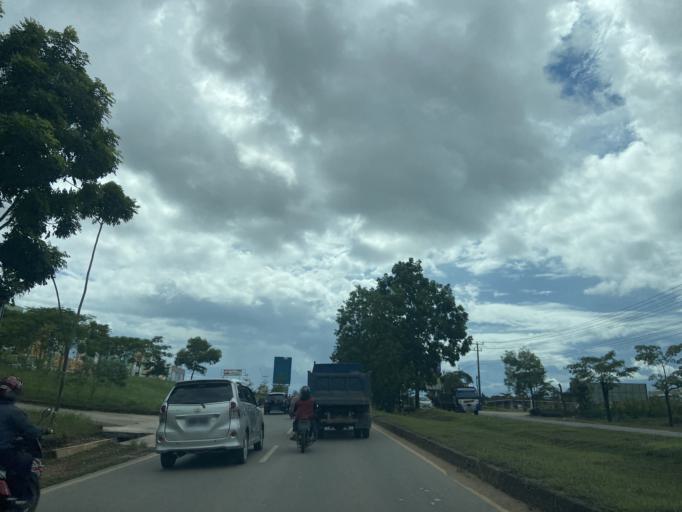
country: SG
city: Singapore
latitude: 1.0398
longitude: 103.9950
